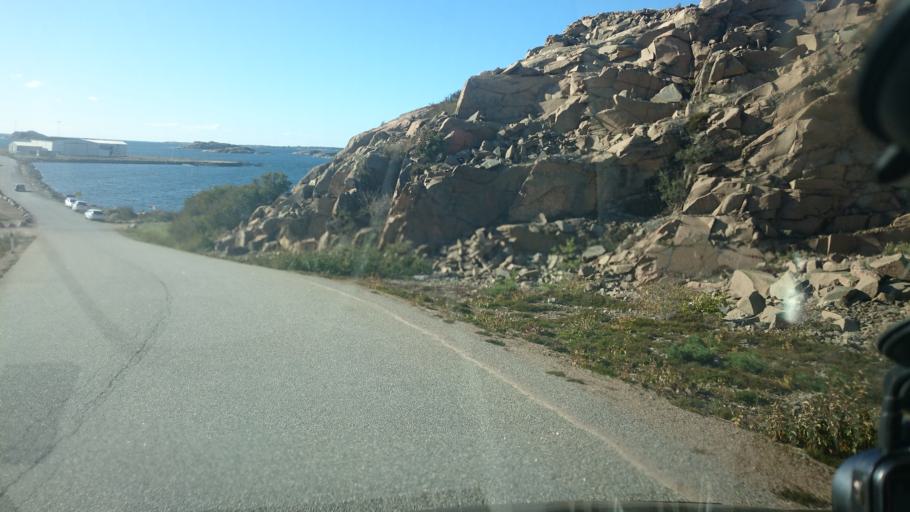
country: SE
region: Vaestra Goetaland
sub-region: Lysekils Kommun
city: Lysekil
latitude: 58.3176
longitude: 11.4030
